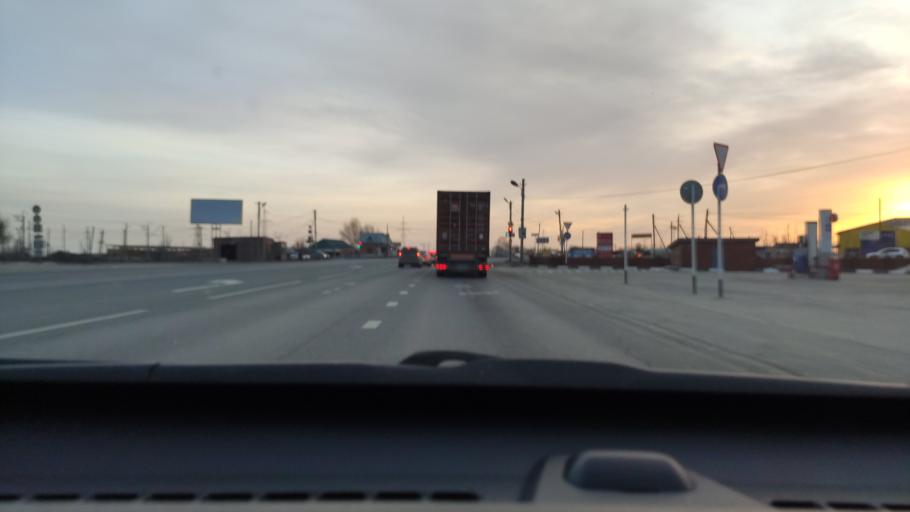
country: RU
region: Samara
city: Tol'yatti
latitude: 53.5772
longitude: 49.4048
